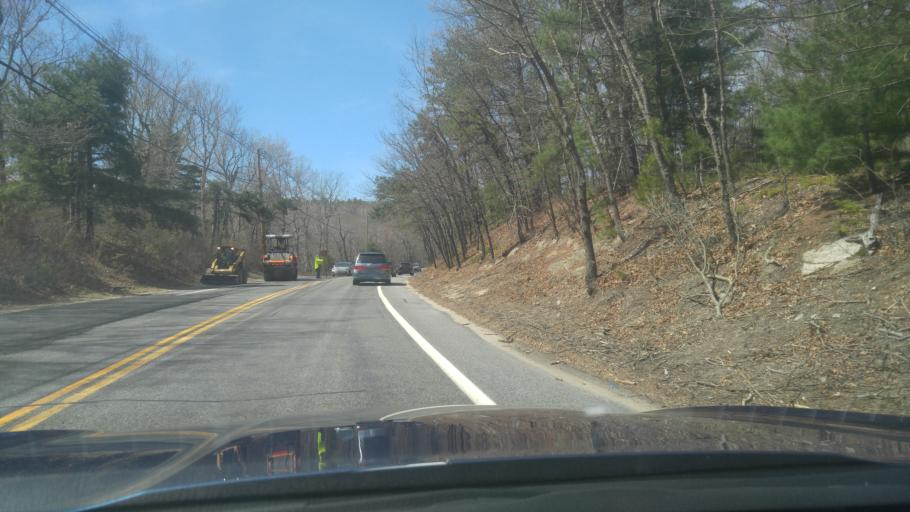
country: US
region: Rhode Island
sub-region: Washington County
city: Exeter
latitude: 41.5795
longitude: -71.6122
